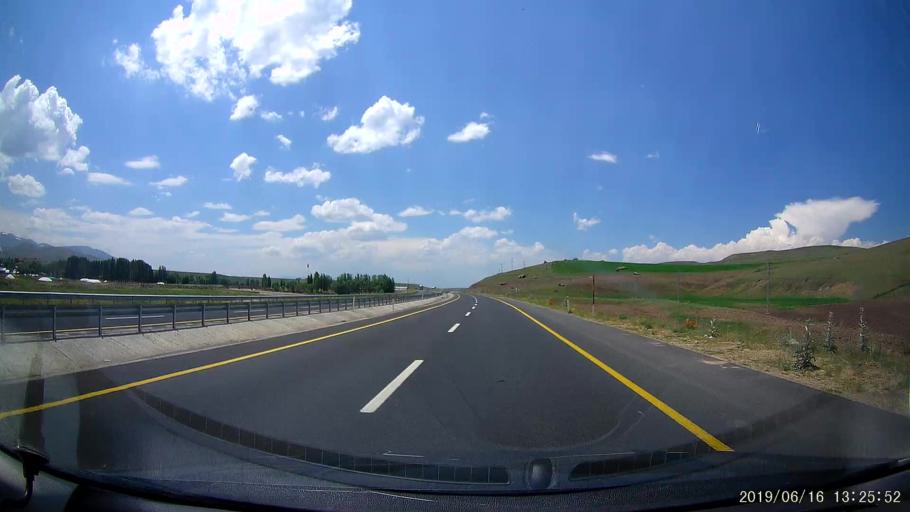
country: TR
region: Agri
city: Taslicay
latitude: 39.6561
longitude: 43.3424
